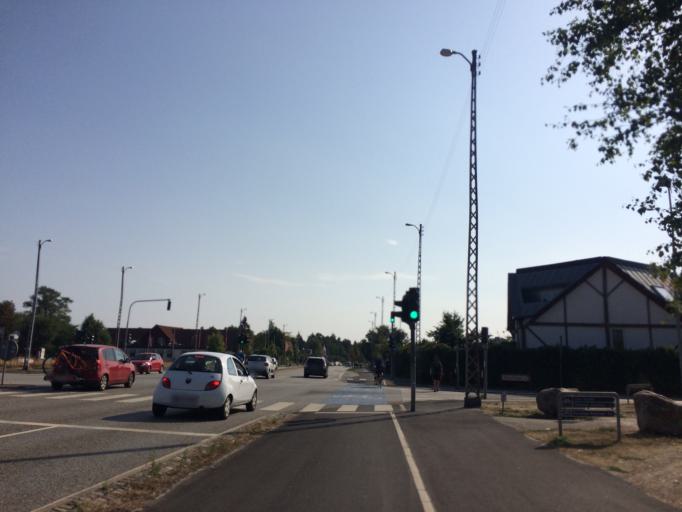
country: DK
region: Capital Region
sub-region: Ishoj Kommune
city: Ishoj
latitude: 55.6011
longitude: 12.3503
